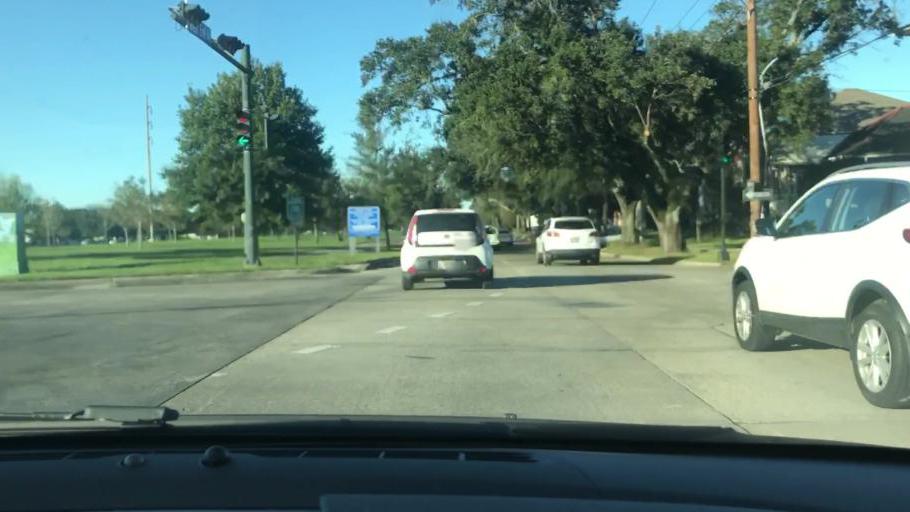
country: US
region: Louisiana
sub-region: Jefferson Parish
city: Metairie
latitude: 30.0001
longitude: -90.1151
